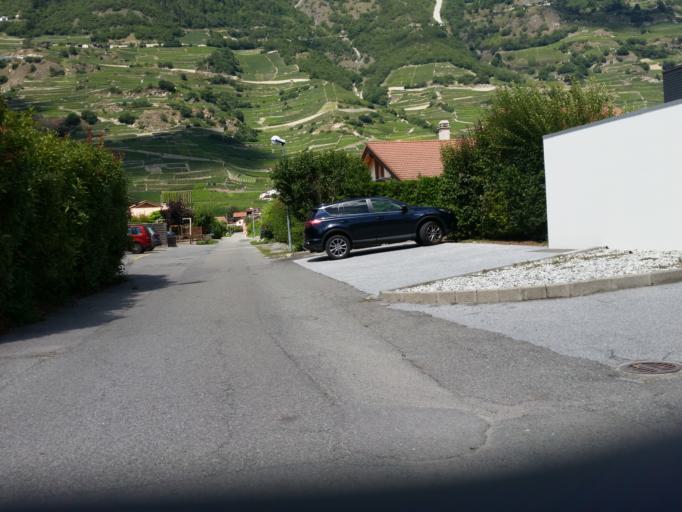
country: CH
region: Valais
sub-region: Martigny District
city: Fully
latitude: 46.1410
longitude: 7.1279
